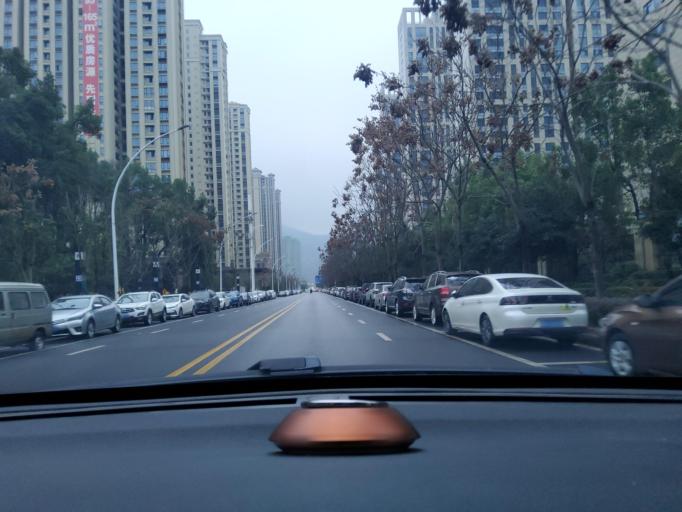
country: CN
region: Hubei
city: Tuanchengshan
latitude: 30.1988
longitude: 115.0093
